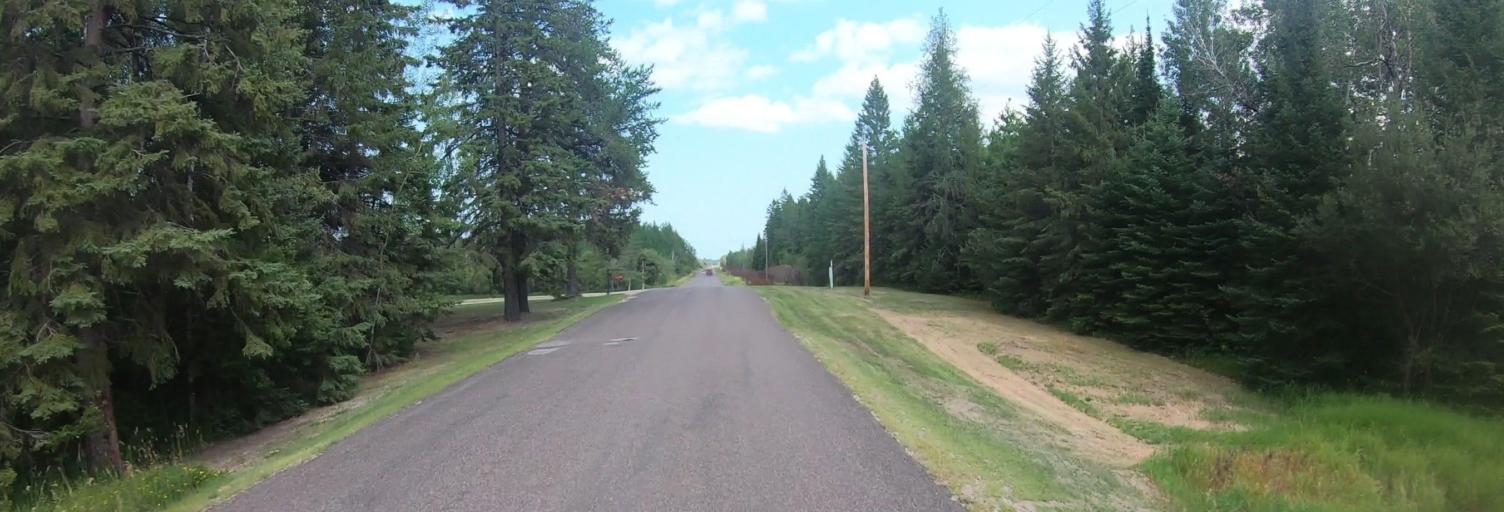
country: US
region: Minnesota
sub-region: Saint Louis County
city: Mountain Iron
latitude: 47.8919
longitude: -92.6917
